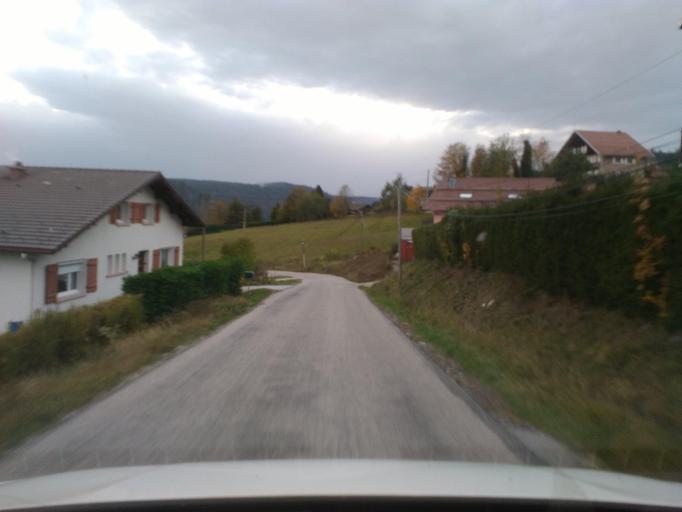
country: FR
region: Lorraine
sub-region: Departement des Vosges
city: Gerardmer
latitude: 48.0801
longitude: 6.8676
